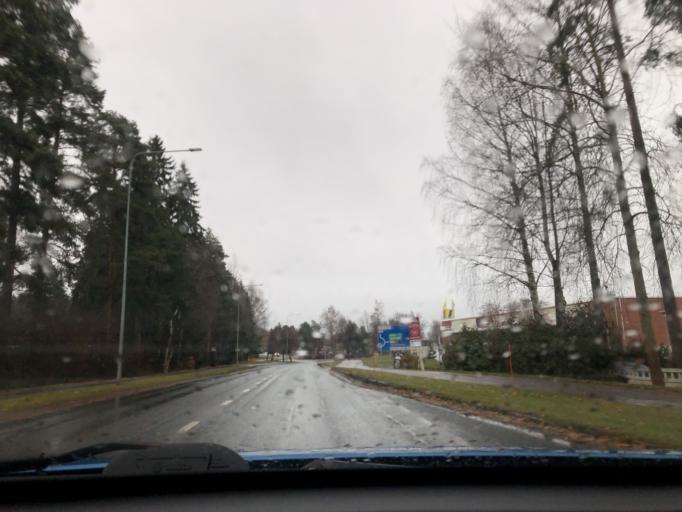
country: FI
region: Pirkanmaa
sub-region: Tampere
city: Kangasala
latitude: 61.4700
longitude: 24.0372
